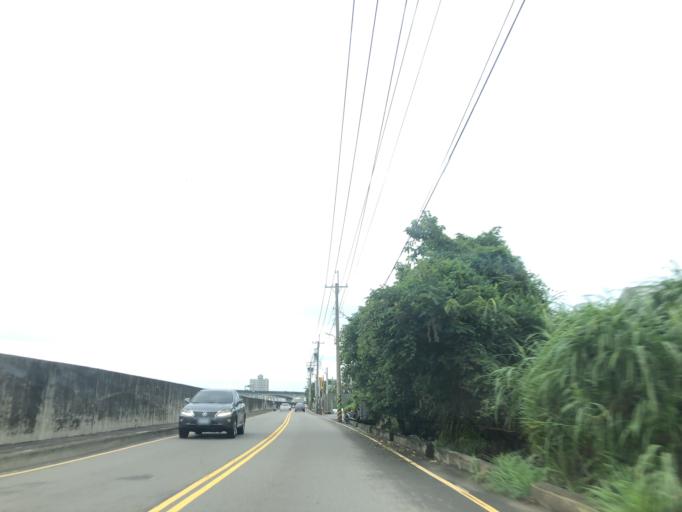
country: TW
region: Taiwan
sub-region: Taichung City
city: Taichung
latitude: 24.1160
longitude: 120.7026
